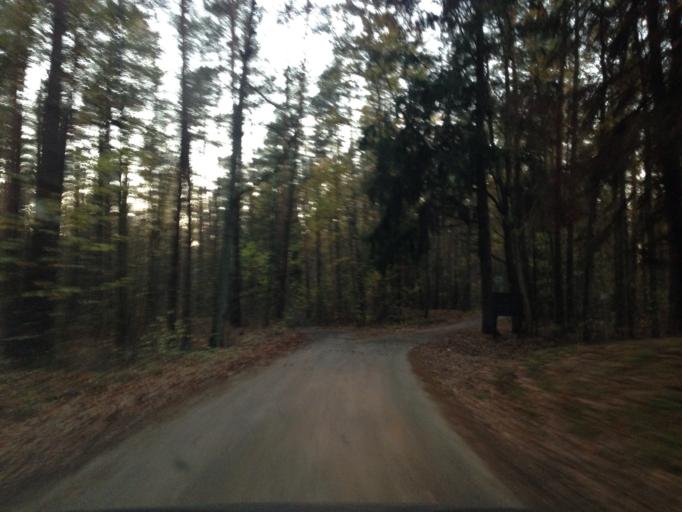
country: PL
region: Kujawsko-Pomorskie
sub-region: Powiat brodnicki
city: Gorzno
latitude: 53.2266
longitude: 19.7116
